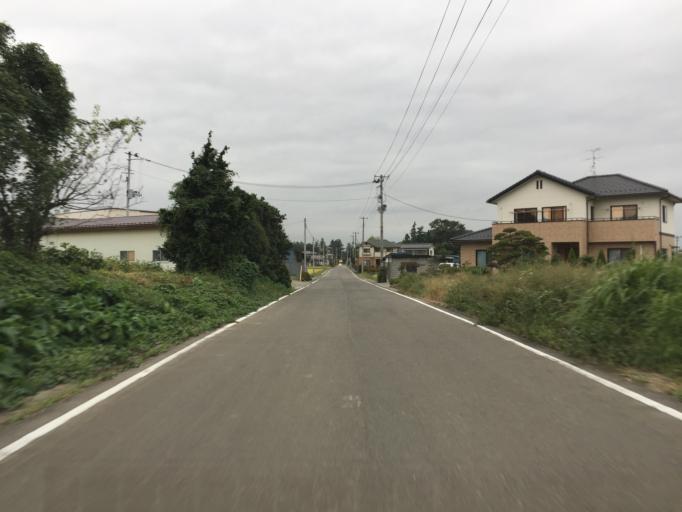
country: JP
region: Fukushima
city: Nihommatsu
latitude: 37.6485
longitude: 140.4605
